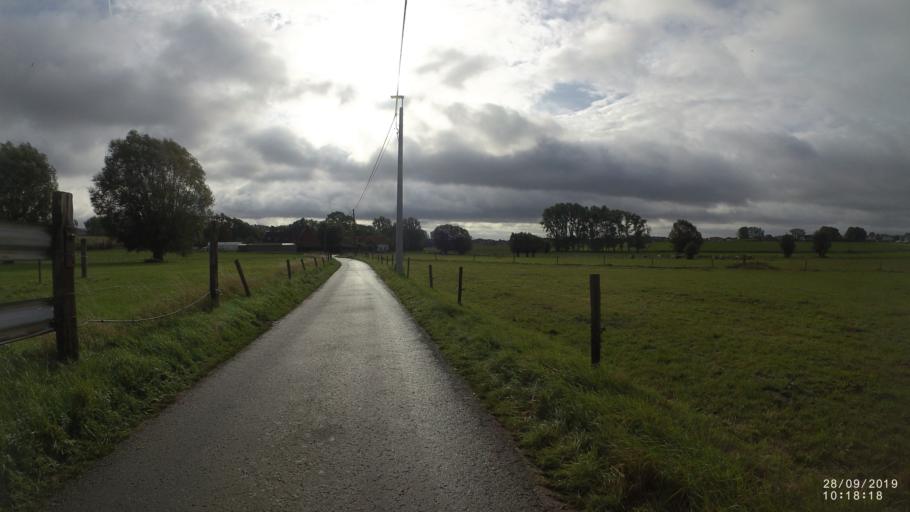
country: BE
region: Flanders
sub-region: Provincie Oost-Vlaanderen
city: Sint-Maria-Lierde
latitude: 50.8098
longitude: 3.8278
